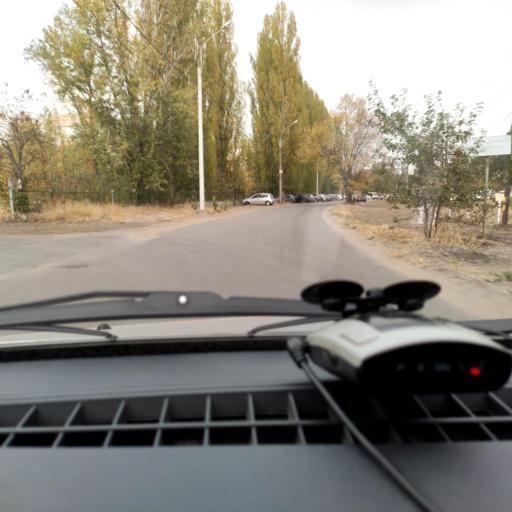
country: RU
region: Voronezj
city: Podgornoye
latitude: 51.7427
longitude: 39.1734
